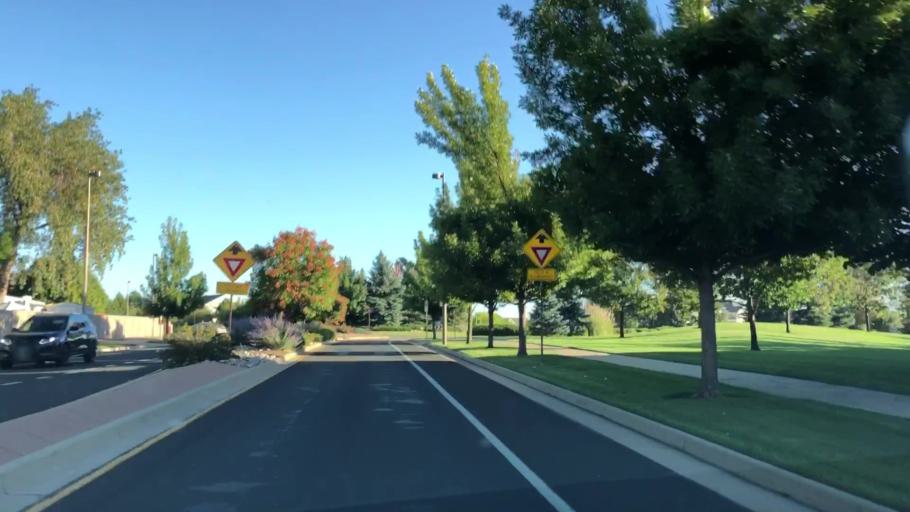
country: US
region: Colorado
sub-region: Larimer County
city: Loveland
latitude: 40.4094
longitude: -105.0114
